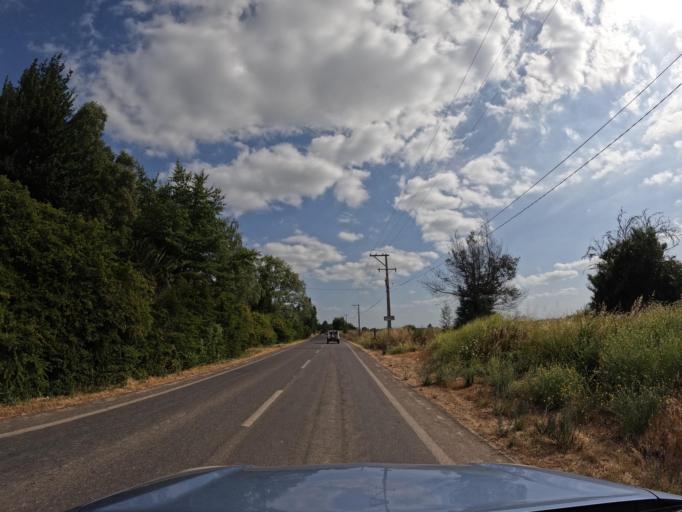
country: CL
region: Maule
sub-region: Provincia de Curico
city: Molina
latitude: -35.1940
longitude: -71.2973
